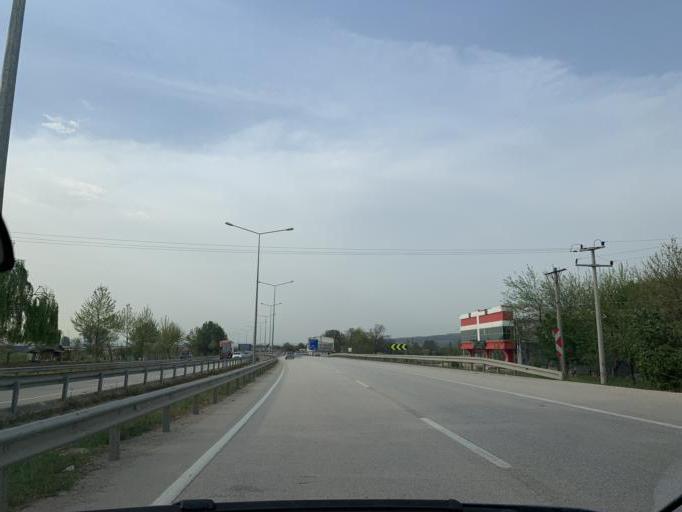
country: TR
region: Bursa
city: Kursunlu
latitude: 40.0541
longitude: 29.5880
